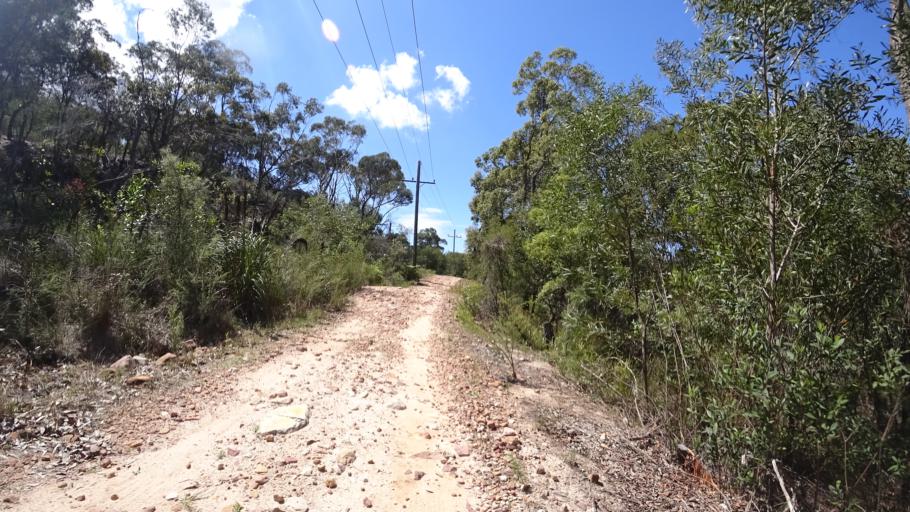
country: AU
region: New South Wales
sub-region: Warringah
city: Killarney Heights
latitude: -33.7621
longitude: 151.2231
